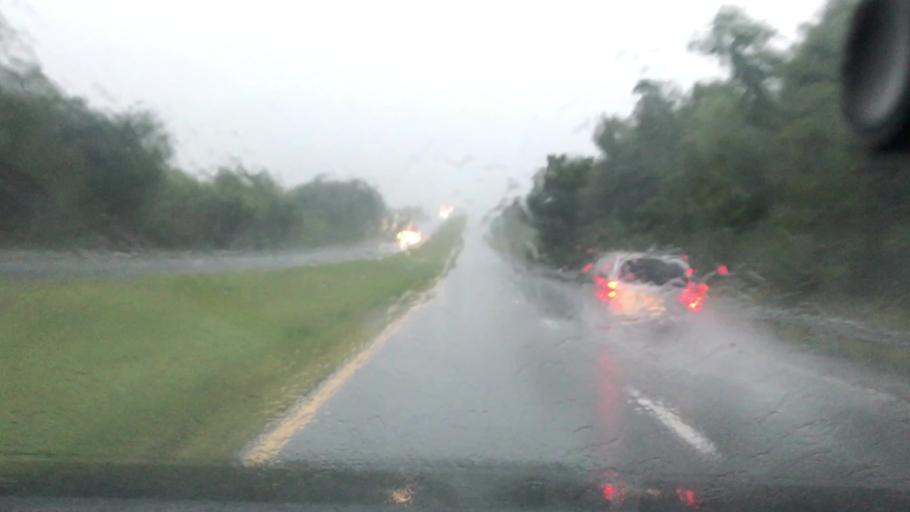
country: US
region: Virginia
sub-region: Giles County
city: Pearisburg
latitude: 37.3352
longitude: -80.7025
